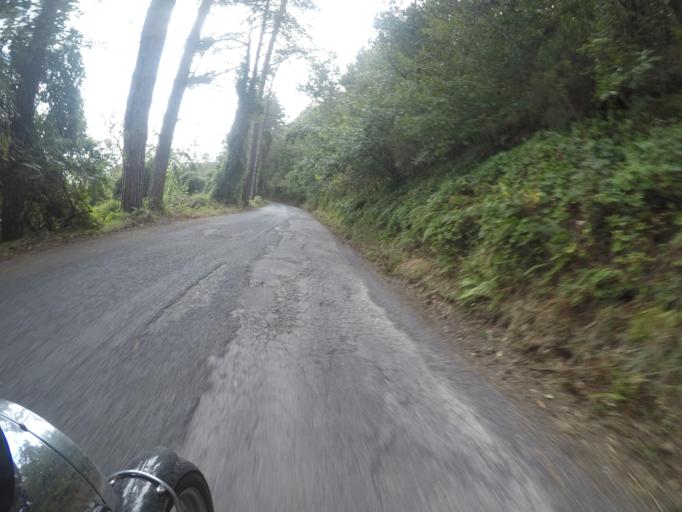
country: IT
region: Tuscany
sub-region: Provincia di Massa-Carrara
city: Fosdinovo
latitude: 44.1233
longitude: 10.0654
